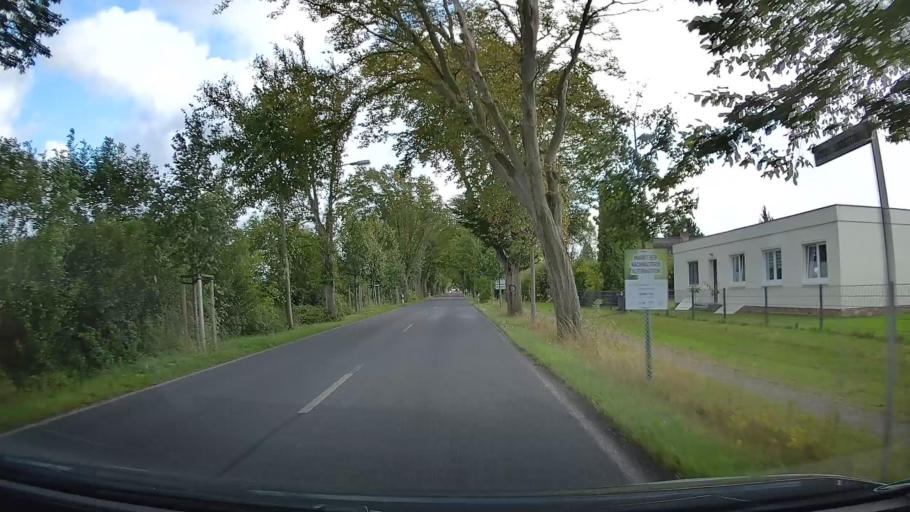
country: DE
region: Mecklenburg-Vorpommern
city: Putbus
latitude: 54.3643
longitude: 13.4778
